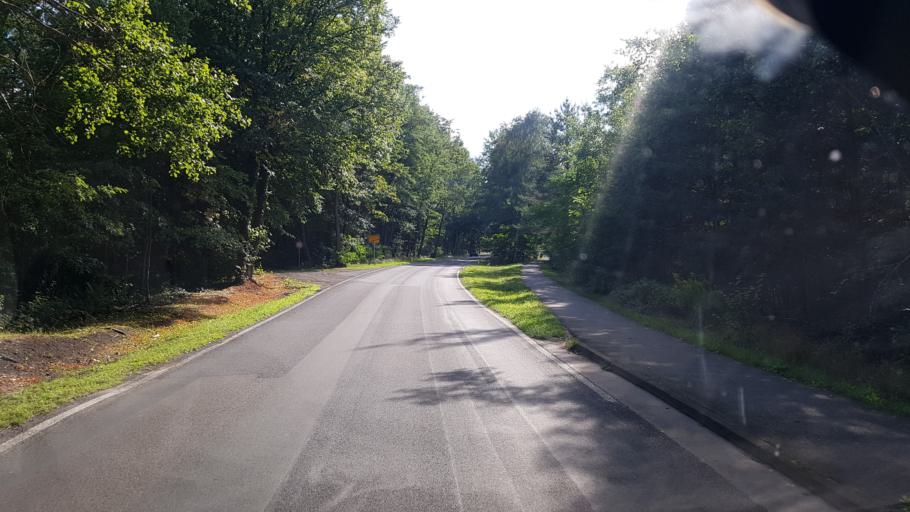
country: DE
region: Brandenburg
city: Tschernitz
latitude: 51.6095
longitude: 14.5895
